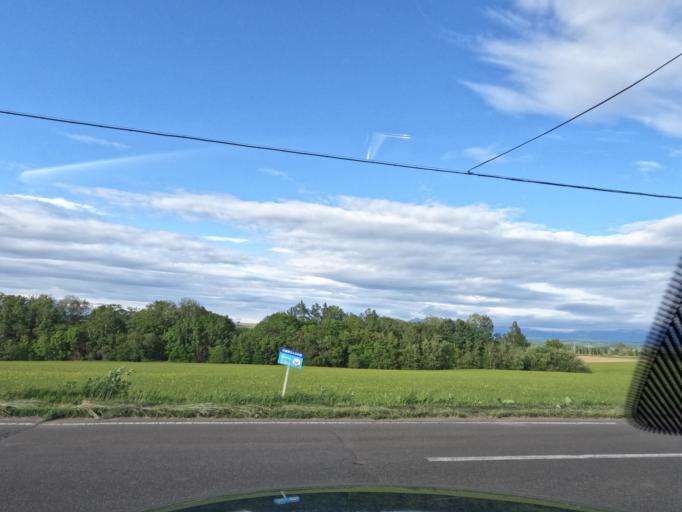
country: JP
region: Hokkaido
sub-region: Asahikawa-shi
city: Asahikawa
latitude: 43.6075
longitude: 142.4593
